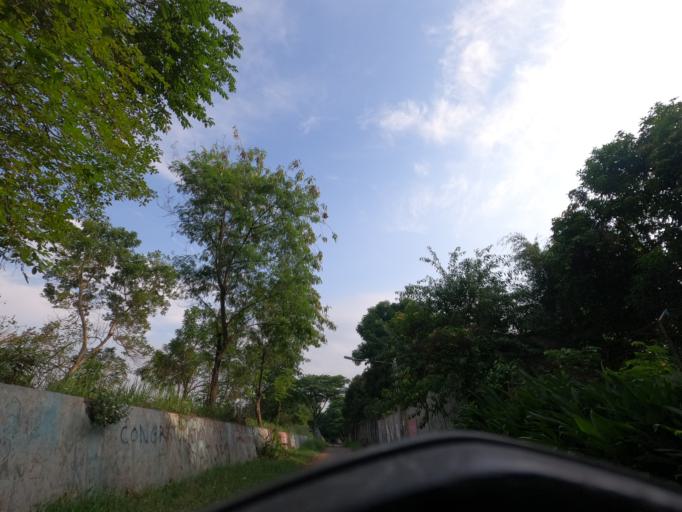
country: ID
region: West Java
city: Lembang
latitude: -6.5774
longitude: 107.7640
